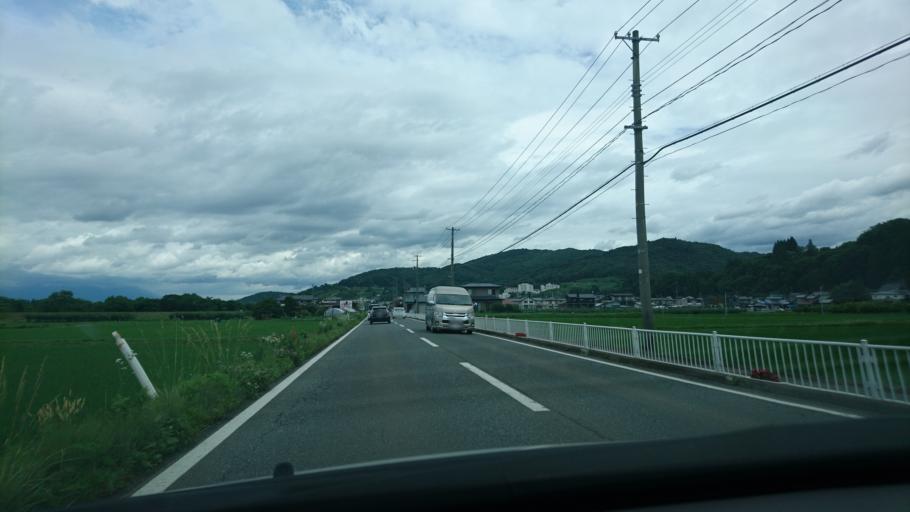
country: JP
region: Iwate
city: Morioka-shi
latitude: 39.6468
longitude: 141.1842
